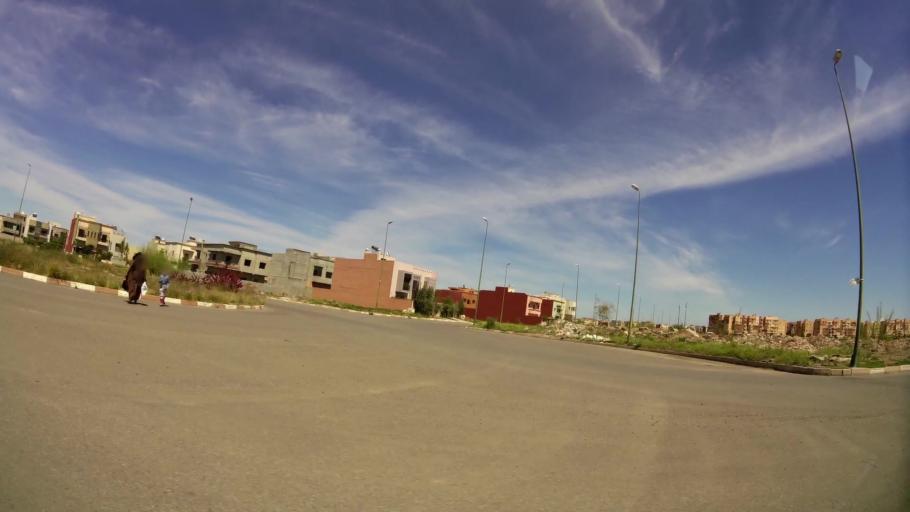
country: MA
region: Marrakech-Tensift-Al Haouz
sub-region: Marrakech
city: Marrakesh
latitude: 31.6495
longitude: -8.0790
